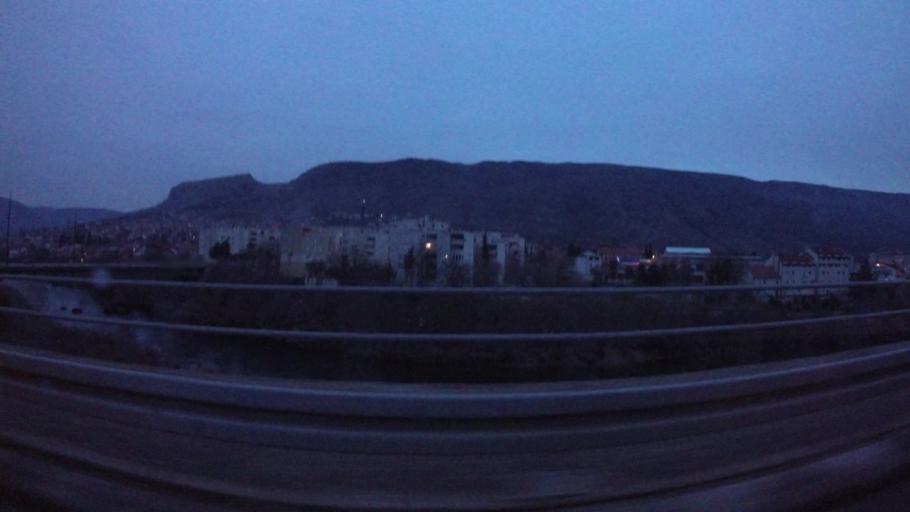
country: BA
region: Federation of Bosnia and Herzegovina
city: Rodoc
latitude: 43.3253
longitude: 17.8190
